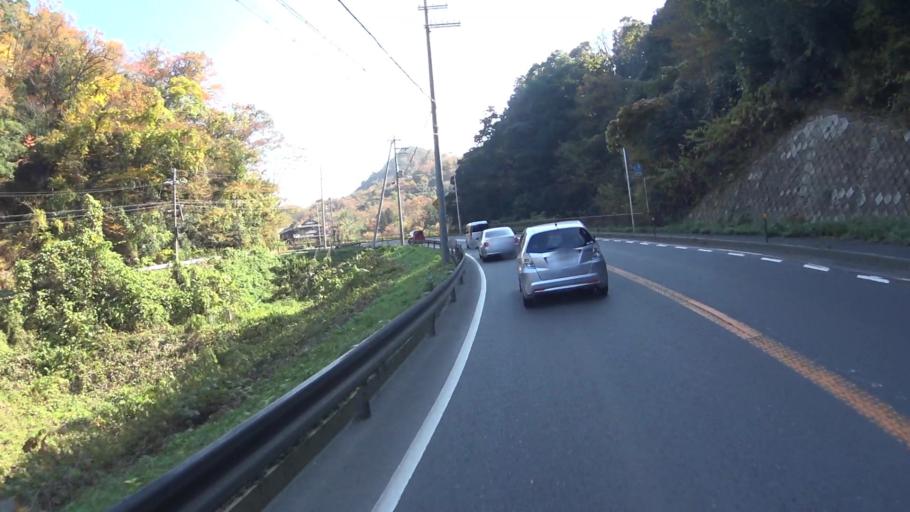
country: JP
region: Kyoto
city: Maizuru
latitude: 35.4486
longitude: 135.2751
